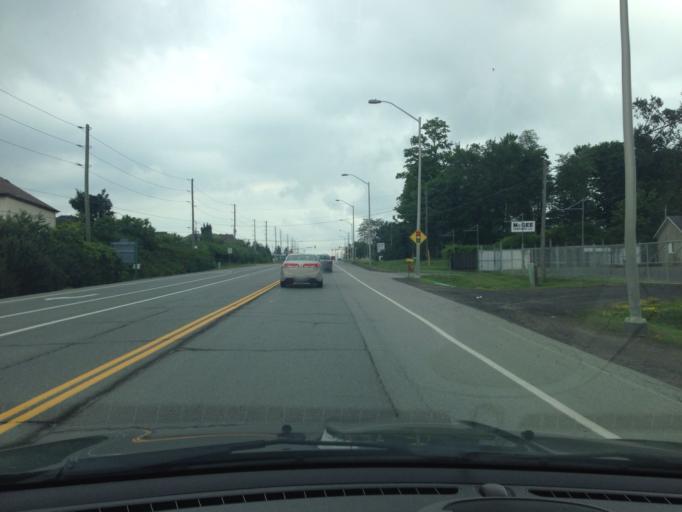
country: CA
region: Ontario
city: Ottawa
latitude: 45.3212
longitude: -75.5941
